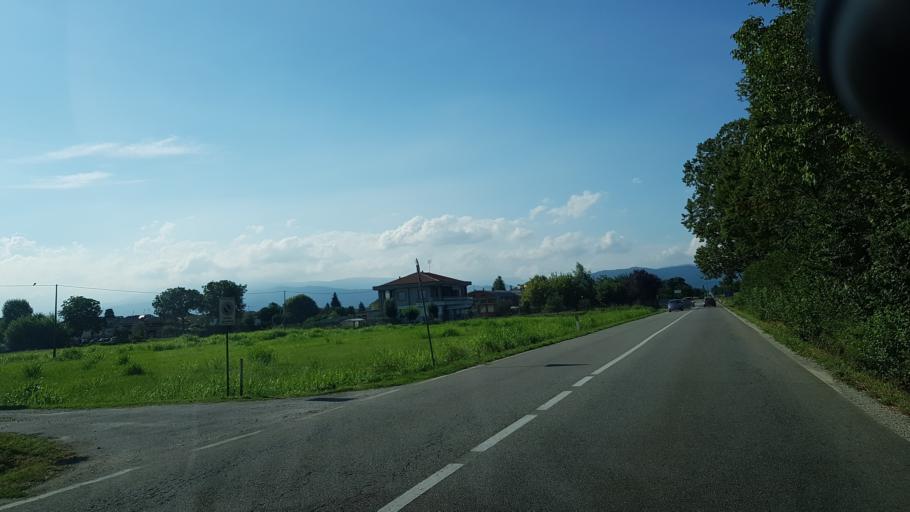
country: IT
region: Piedmont
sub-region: Provincia di Cuneo
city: Roata Rossi
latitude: 44.4439
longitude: 7.5299
